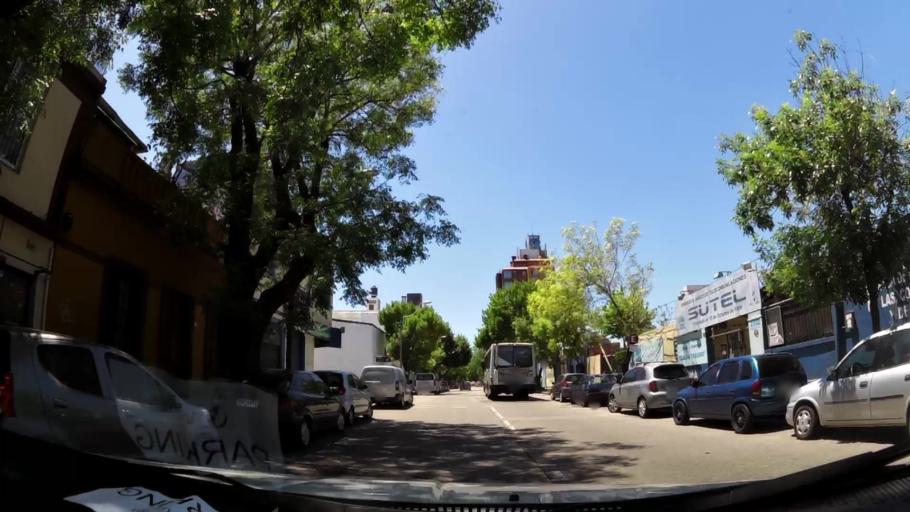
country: UY
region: Montevideo
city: Montevideo
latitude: -34.8919
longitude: -56.1686
